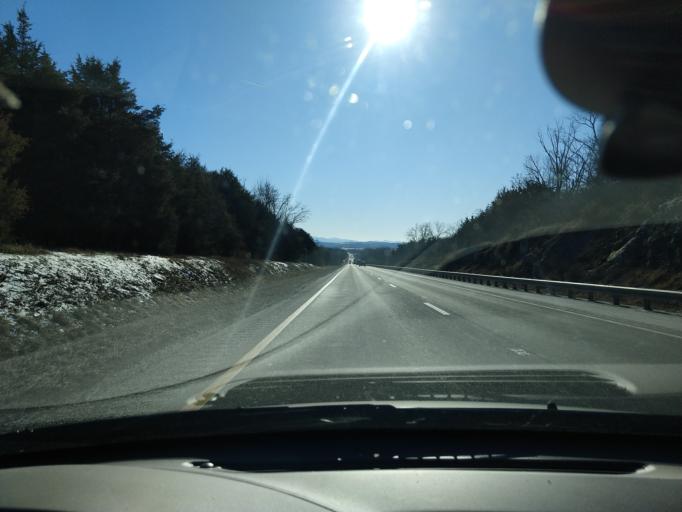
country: US
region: Virginia
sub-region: Rockbridge County
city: East Lexington
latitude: 37.8287
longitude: -79.3745
